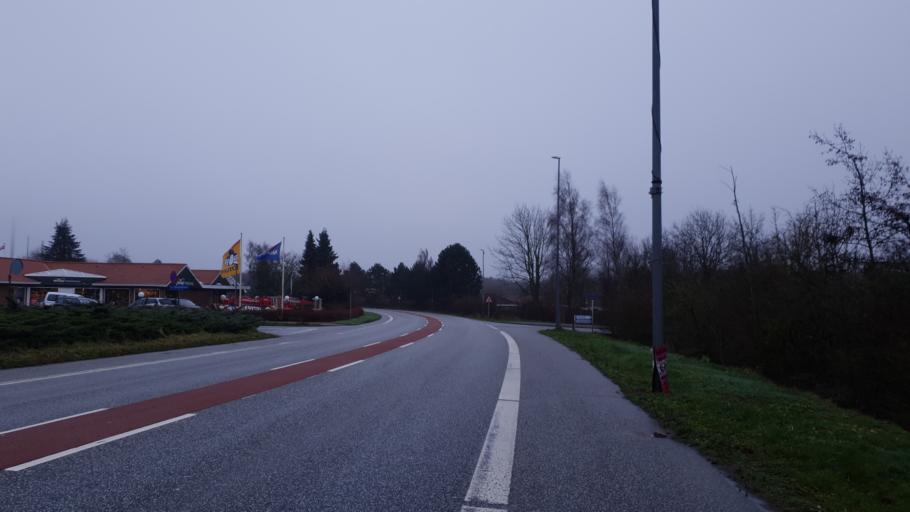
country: DK
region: Central Jutland
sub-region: Hedensted Kommune
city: Hedensted
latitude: 55.7778
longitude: 9.6959
